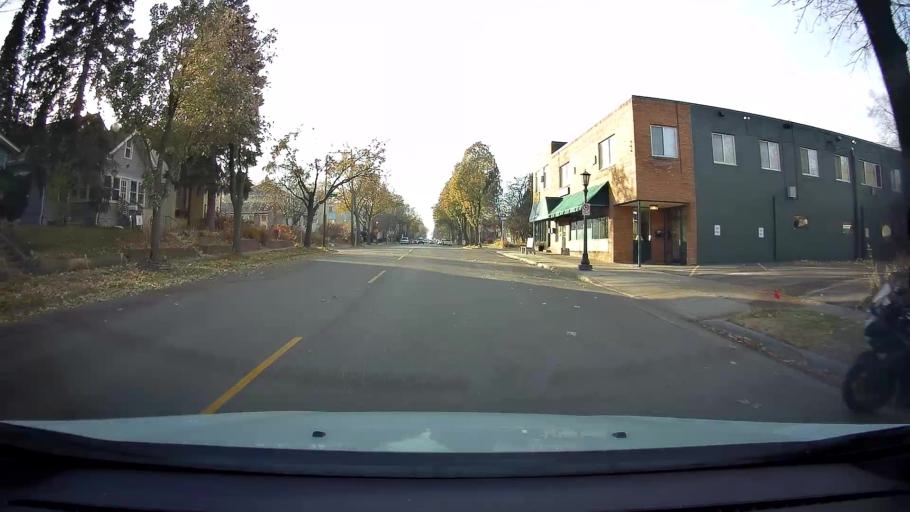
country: US
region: Minnesota
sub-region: Dakota County
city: Mendota Heights
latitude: 44.9342
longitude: -93.1537
